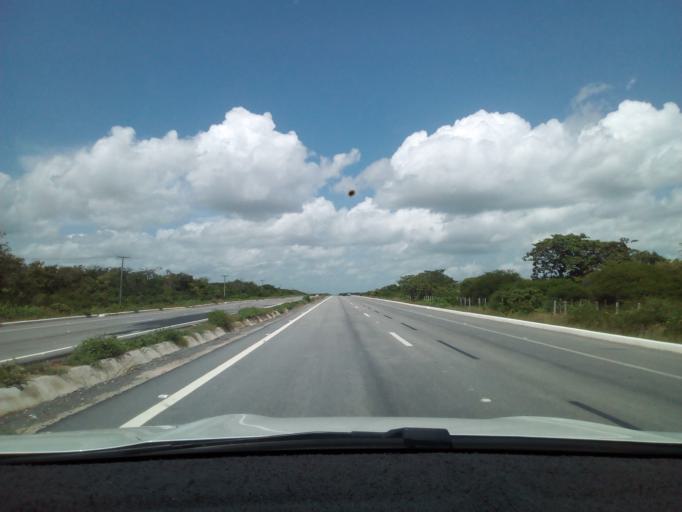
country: BR
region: Ceara
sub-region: Aracati
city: Aracati
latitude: -4.5163
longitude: -37.7998
